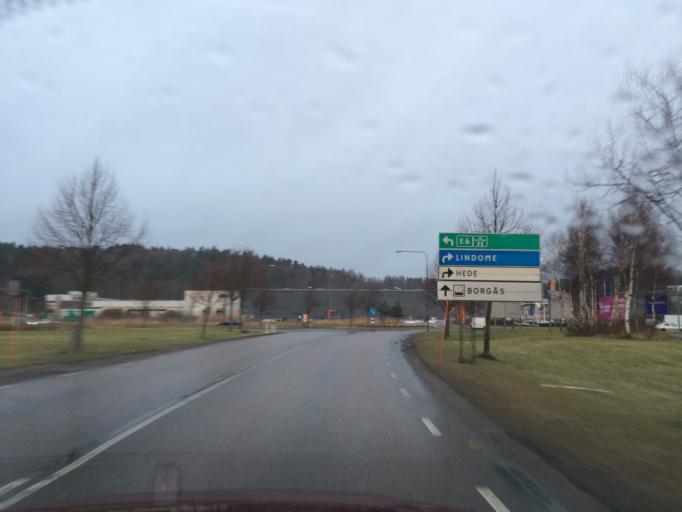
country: SE
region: Halland
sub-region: Kungsbacka Kommun
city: Kungsbacka
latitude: 57.5081
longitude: 12.0640
